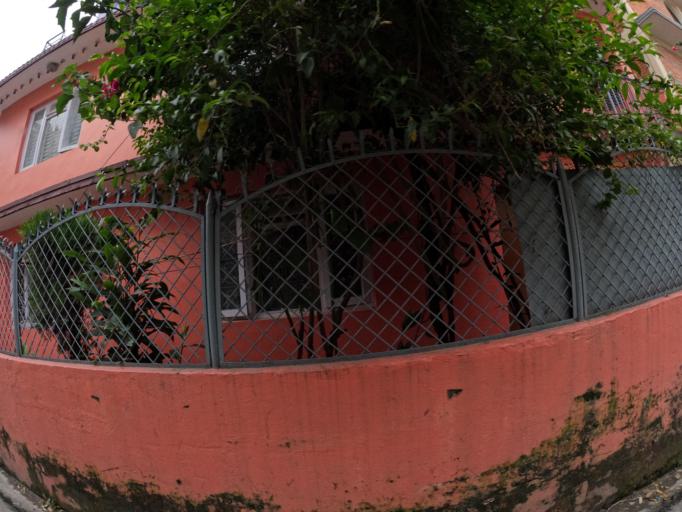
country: NP
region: Central Region
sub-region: Bagmati Zone
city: Kathmandu
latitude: 27.7429
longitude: 85.3161
